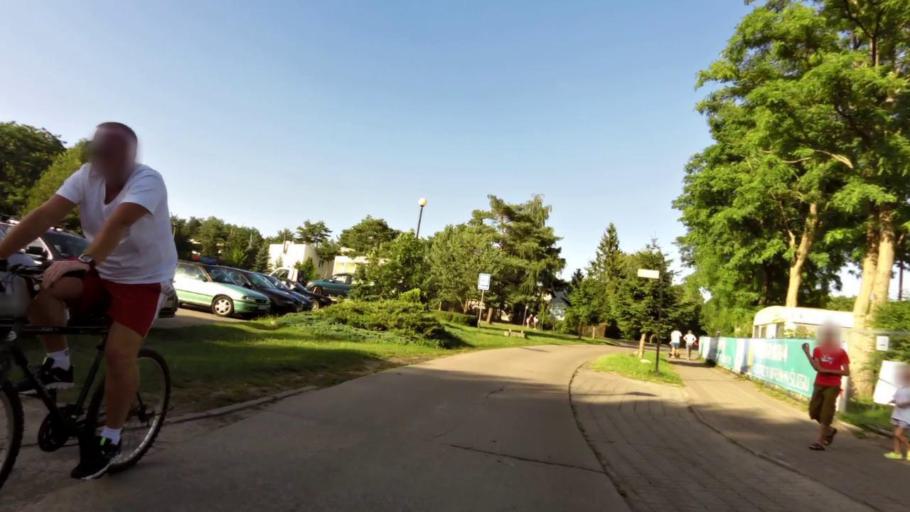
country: PL
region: West Pomeranian Voivodeship
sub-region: Powiat slawienski
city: Darlowo
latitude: 54.3769
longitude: 16.3104
